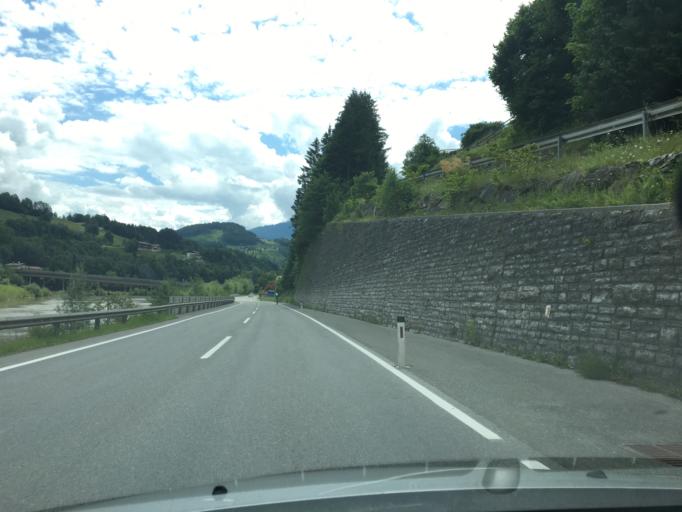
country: AT
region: Salzburg
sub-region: Politischer Bezirk Sankt Johann im Pongau
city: Werfen
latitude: 47.4693
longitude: 13.1942
